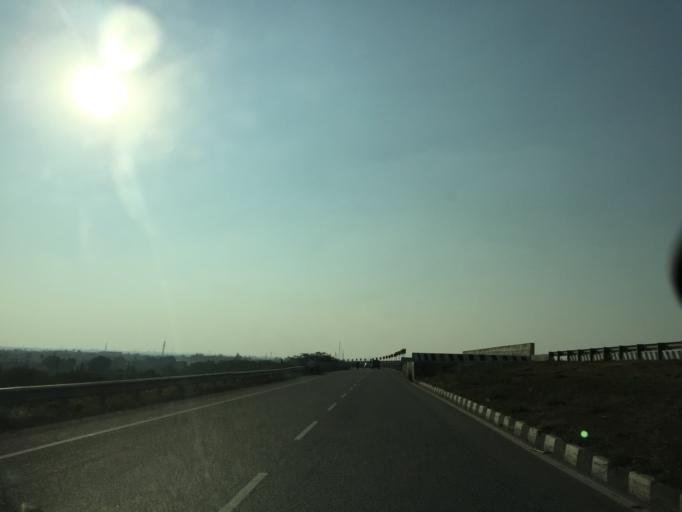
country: IN
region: Telangana
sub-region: Nalgonda
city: Gudur
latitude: 17.5027
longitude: 78.8524
